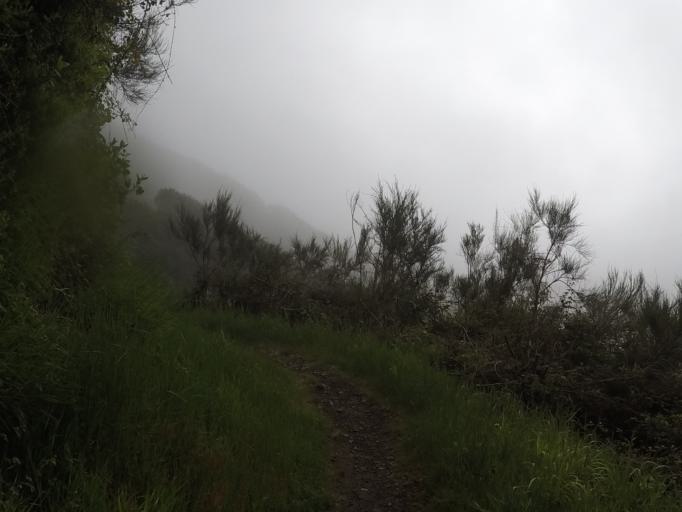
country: PT
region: Madeira
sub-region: Camara de Lobos
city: Curral das Freiras
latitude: 32.7332
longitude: -16.9868
